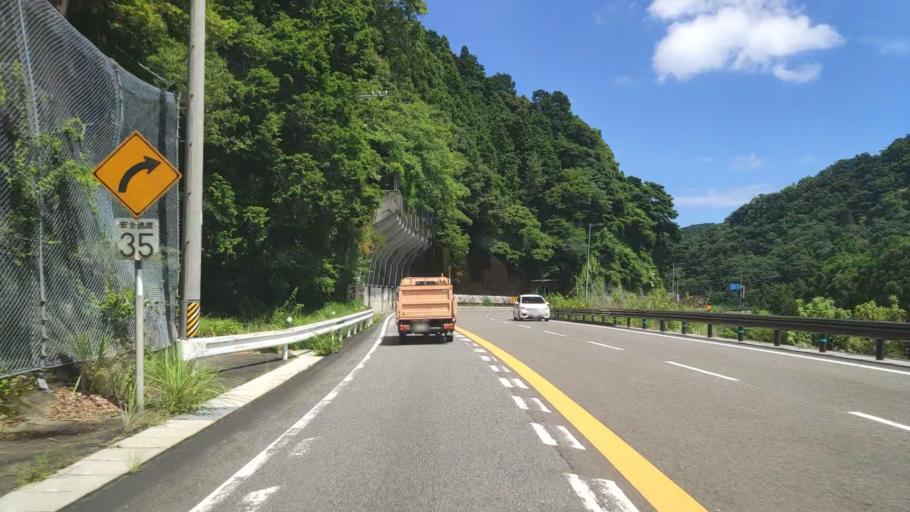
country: JP
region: Mie
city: Owase
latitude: 33.9228
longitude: 136.0956
